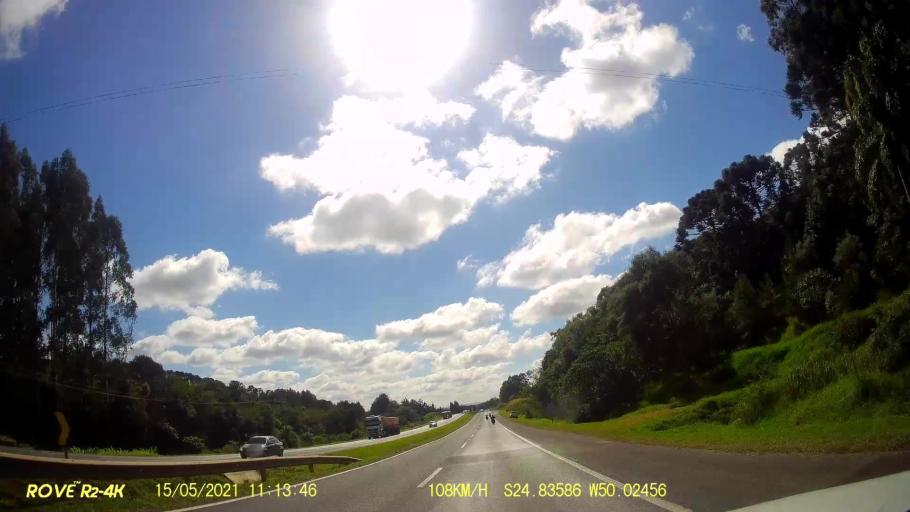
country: BR
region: Parana
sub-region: Castro
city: Castro
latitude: -24.8360
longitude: -50.0248
